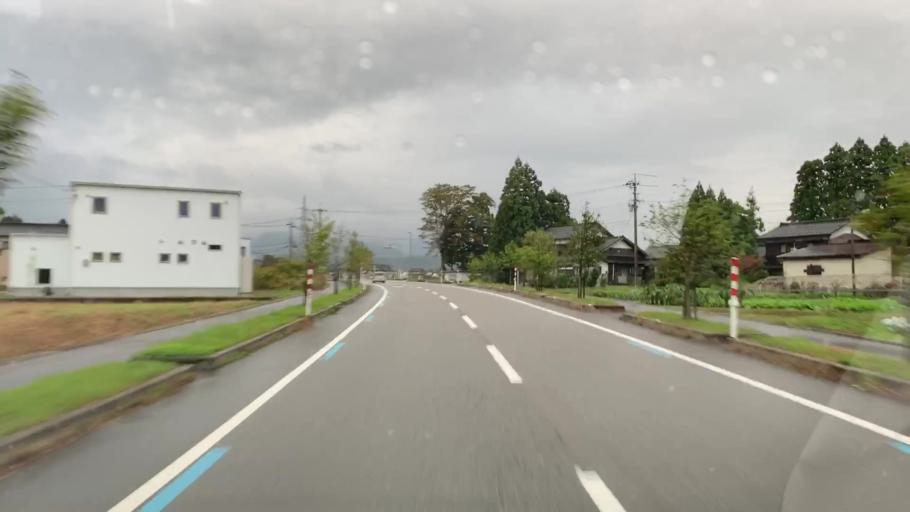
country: JP
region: Toyama
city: Kamiichi
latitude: 36.6137
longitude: 137.3251
